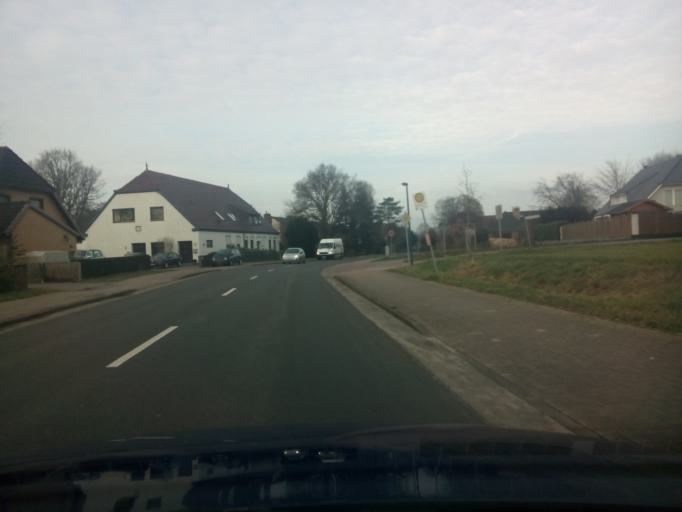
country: DE
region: Lower Saxony
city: Oyten
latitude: 53.0671
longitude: 9.0201
